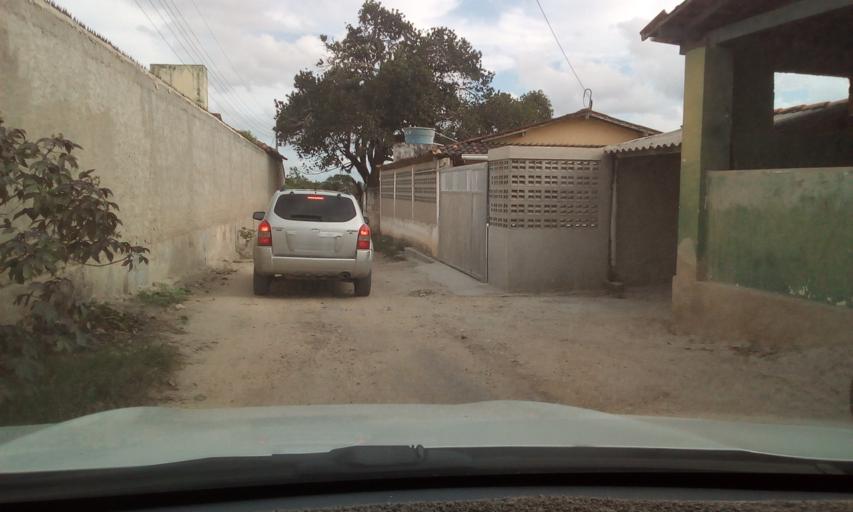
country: BR
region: Pernambuco
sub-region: Cha Grande
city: Cha Grande
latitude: -8.1943
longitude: -35.4958
